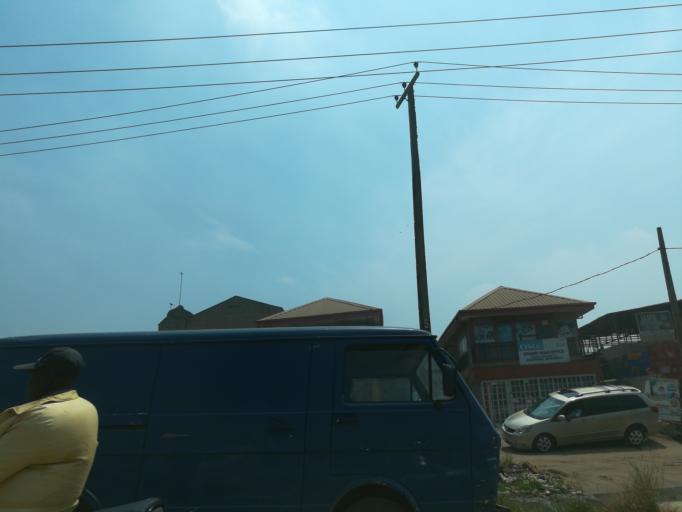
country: NG
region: Lagos
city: Ikorodu
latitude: 6.6393
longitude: 3.4812
